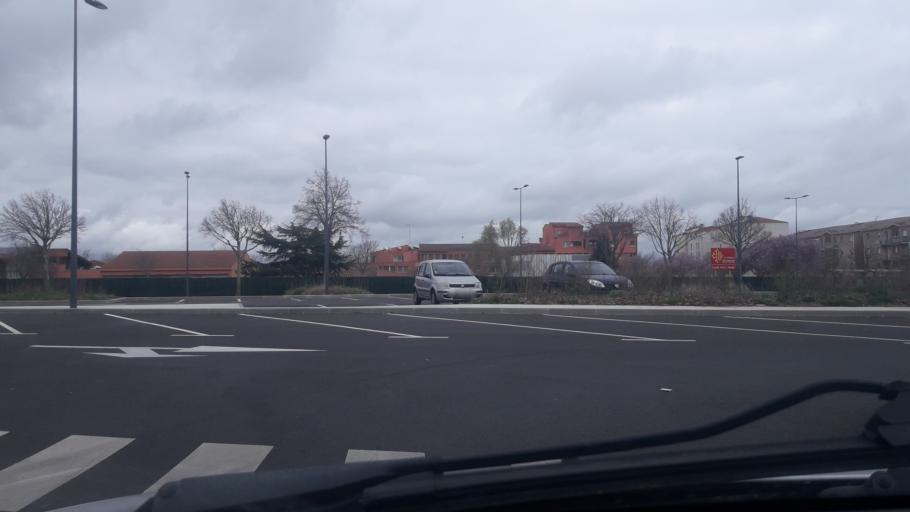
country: FR
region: Midi-Pyrenees
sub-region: Departement de la Haute-Garonne
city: Colomiers
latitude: 43.6143
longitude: 1.3091
